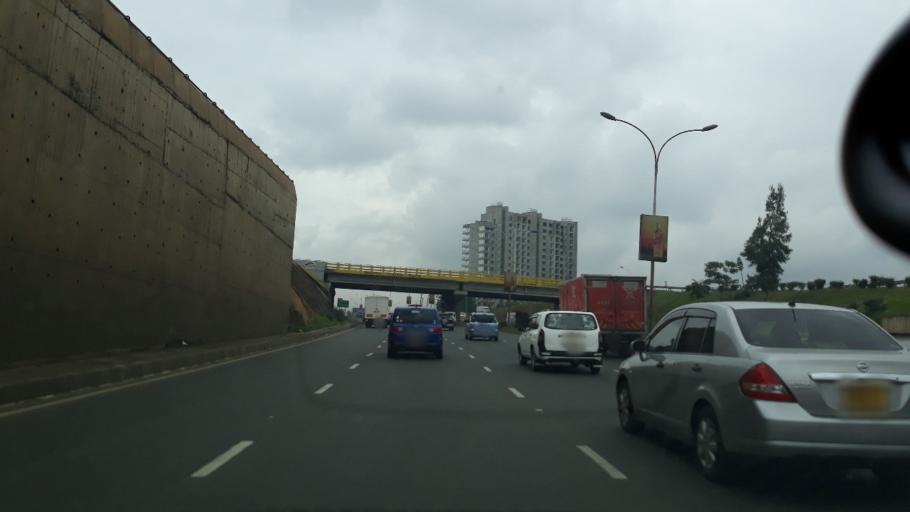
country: KE
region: Nairobi Area
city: Pumwani
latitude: -1.2629
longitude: 36.8393
